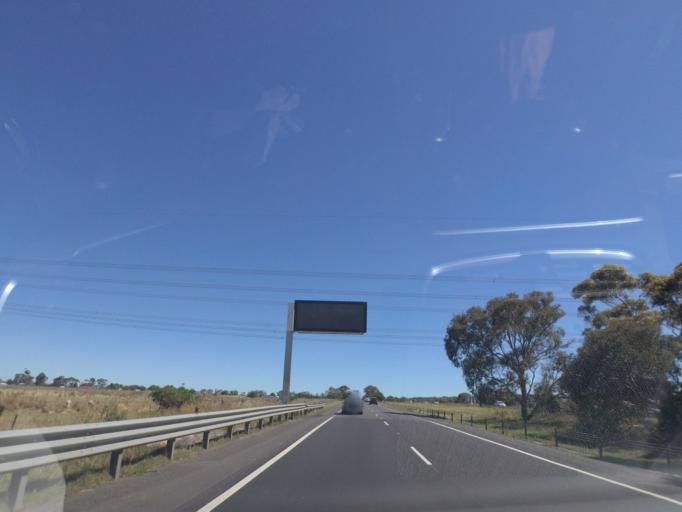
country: AU
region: Victoria
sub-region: Hume
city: Craigieburn
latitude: -37.5542
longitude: 144.9434
